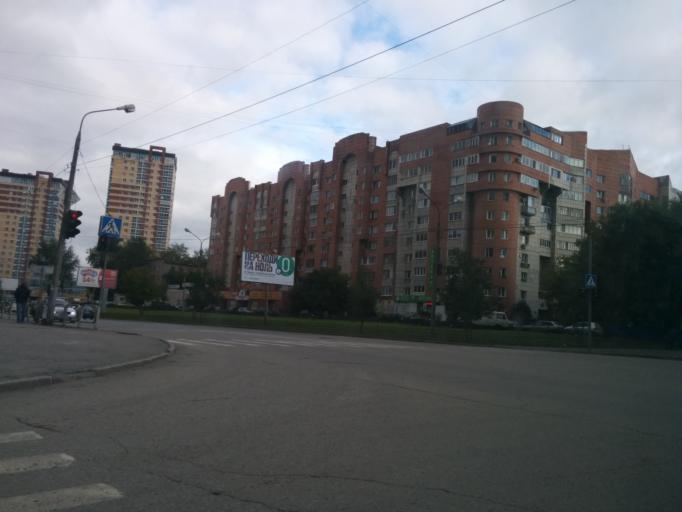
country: RU
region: Perm
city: Perm
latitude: 58.0013
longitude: 56.2995
